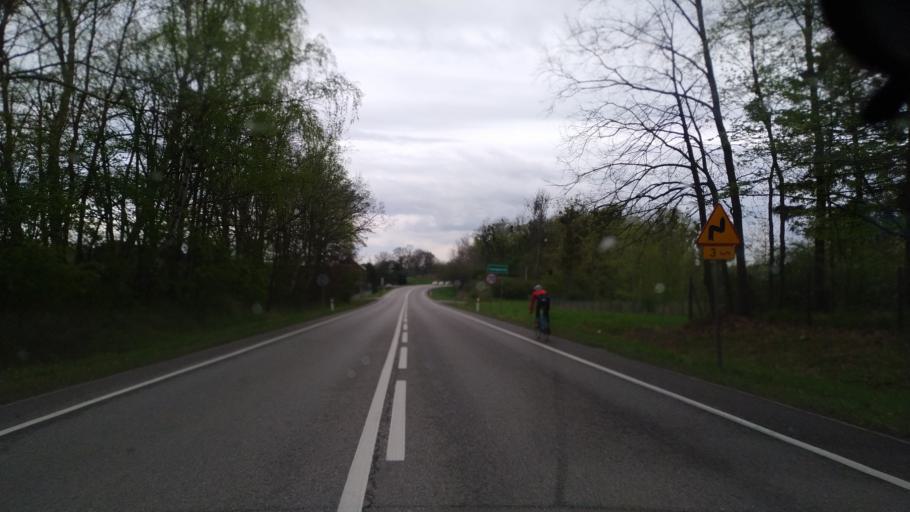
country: PL
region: Pomeranian Voivodeship
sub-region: Powiat starogardzki
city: Starogard Gdanski
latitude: 54.0015
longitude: 18.5964
